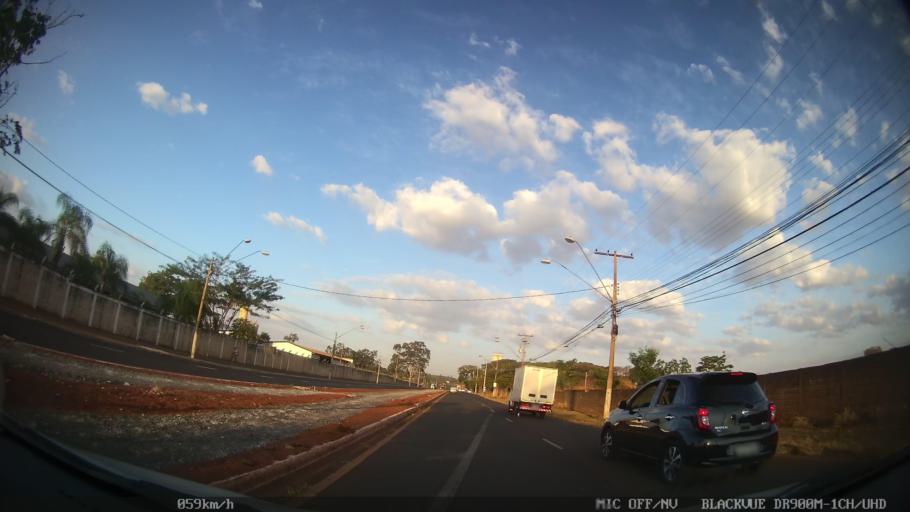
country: BR
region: Sao Paulo
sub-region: Ribeirao Preto
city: Ribeirao Preto
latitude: -21.1483
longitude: -47.7623
